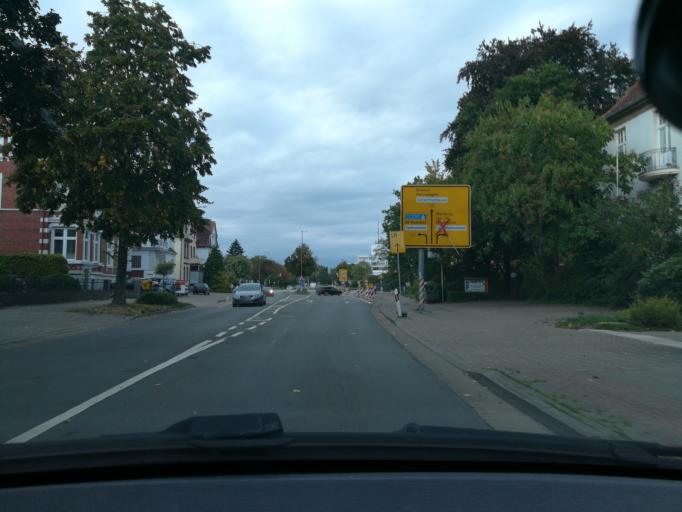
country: DE
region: North Rhine-Westphalia
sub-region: Regierungsbezirk Detmold
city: Minden
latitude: 52.2983
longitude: 8.9158
